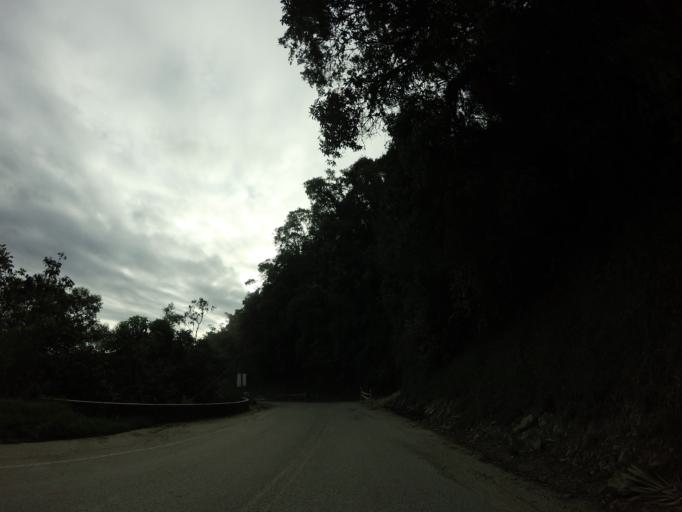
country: CO
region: Tolima
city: Herveo
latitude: 5.1195
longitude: -75.2078
